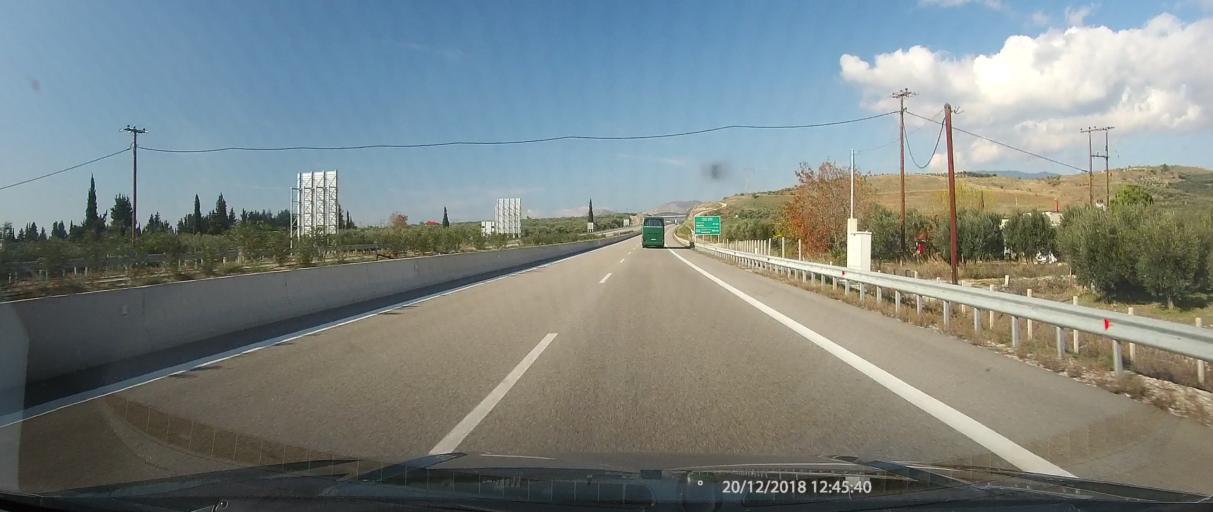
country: GR
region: West Greece
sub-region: Nomos Aitolias kai Akarnanias
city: Mesolongi
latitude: 38.3831
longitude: 21.4904
